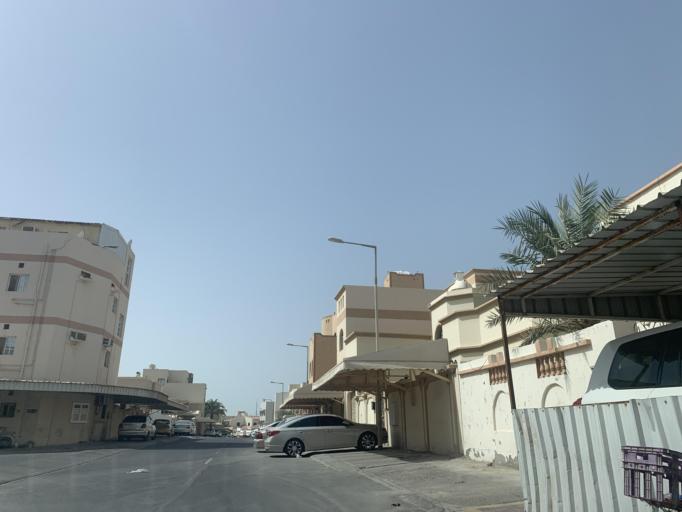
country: BH
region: Northern
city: Ar Rifa'
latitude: 26.1425
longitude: 50.5700
